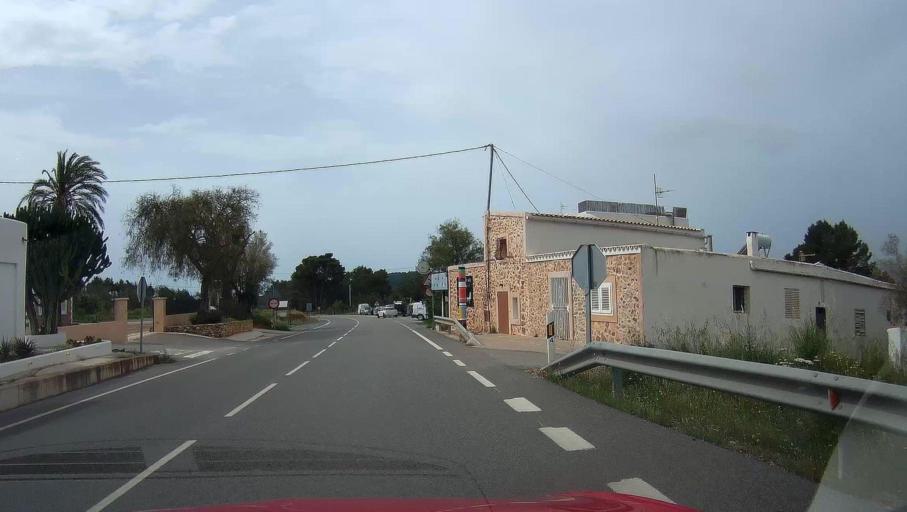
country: ES
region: Balearic Islands
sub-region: Illes Balears
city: Sant Joan de Labritja
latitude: 39.0674
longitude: 1.4947
